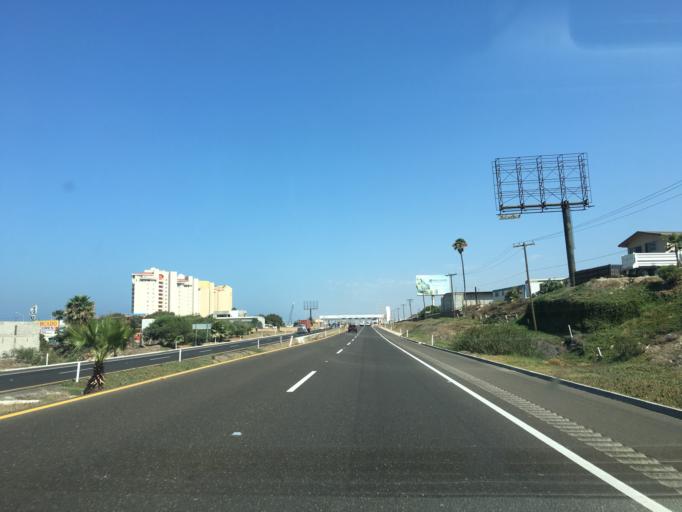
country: MX
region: Baja California
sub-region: Playas de Rosarito
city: Ciudad Morelos
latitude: 32.3067
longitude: -117.0425
